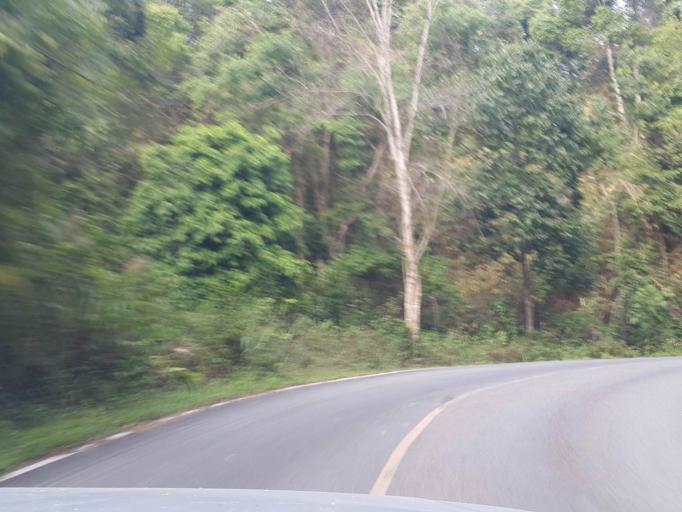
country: TH
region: Chiang Mai
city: Mae On
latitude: 18.9351
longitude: 99.3487
